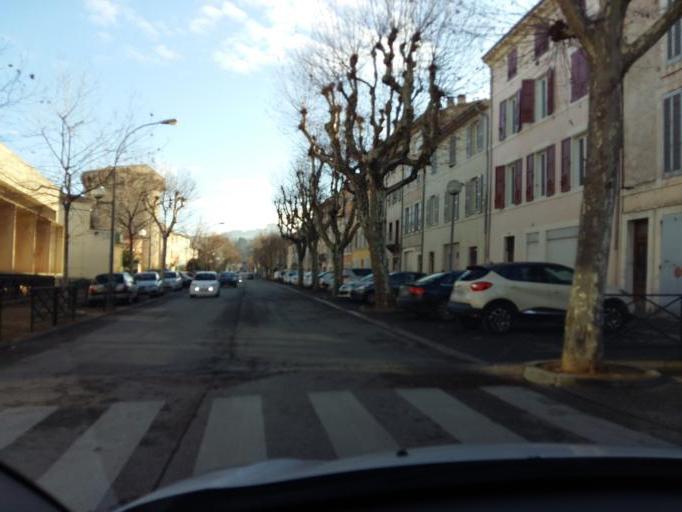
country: FR
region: Provence-Alpes-Cote d'Azur
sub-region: Departement du Vaucluse
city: Apt
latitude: 43.8743
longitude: 5.3953
